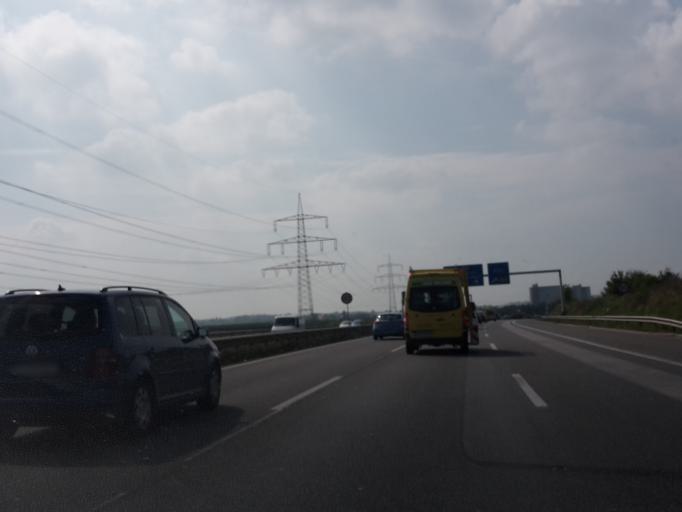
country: DE
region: Rheinland-Pfalz
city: Mainz
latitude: 49.9658
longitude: 8.2489
